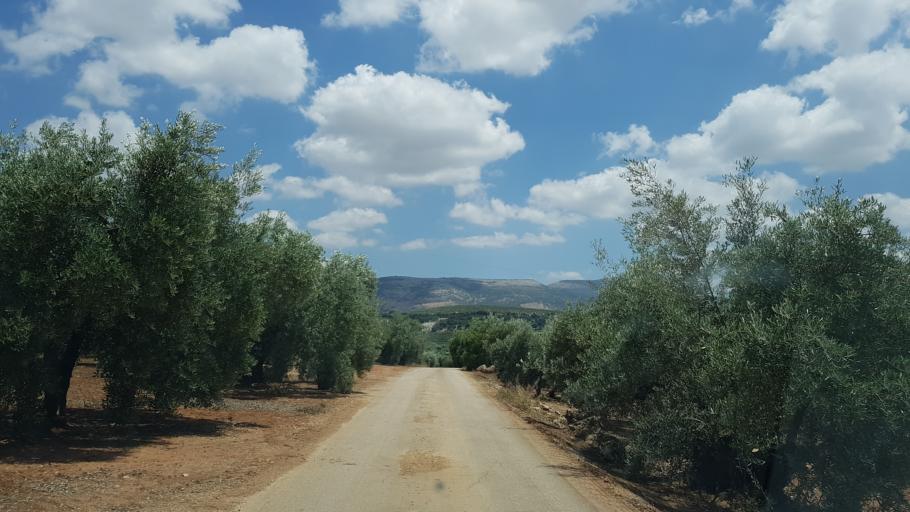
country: ES
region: Andalusia
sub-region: Province of Cordoba
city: Cabra
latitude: 37.5172
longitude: -4.4543
